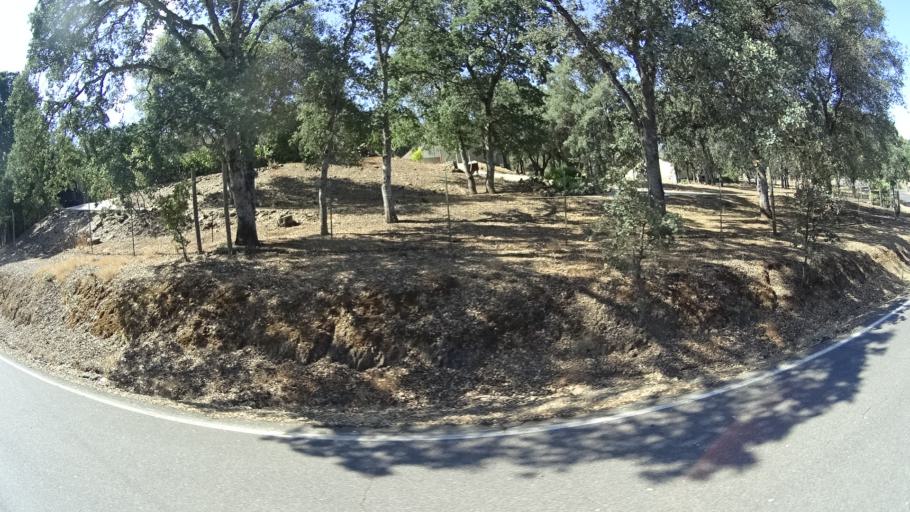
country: US
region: California
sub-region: Calaveras County
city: Copperopolis
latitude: 37.9338
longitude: -120.6358
